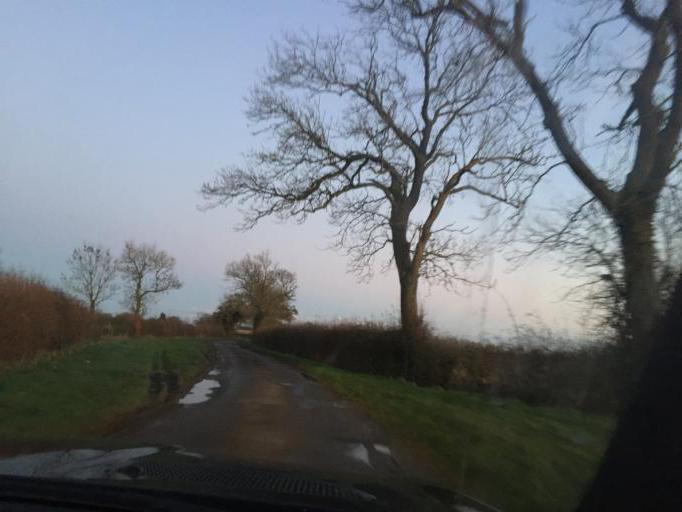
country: GB
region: England
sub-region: Northamptonshire
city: Brackley
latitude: 52.0897
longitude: -1.1031
